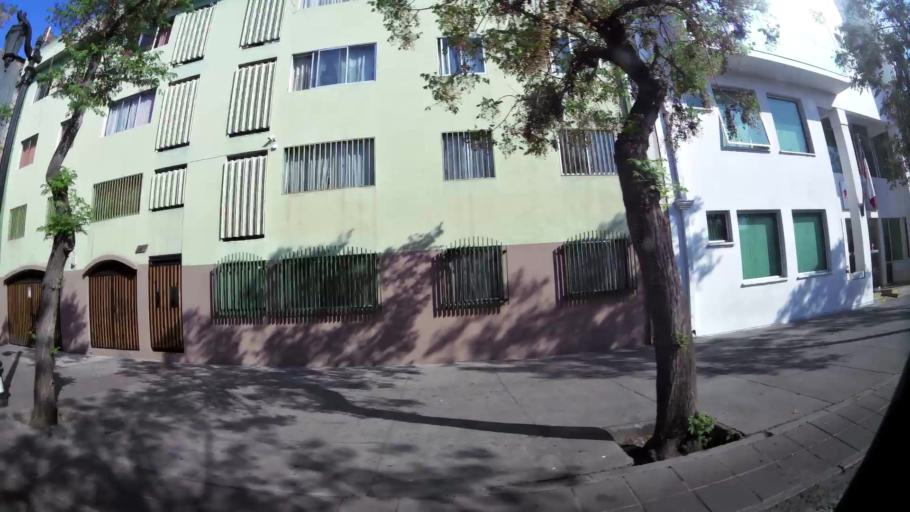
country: CL
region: Santiago Metropolitan
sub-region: Provincia de Santiago
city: Santiago
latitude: -33.4409
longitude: -70.6627
